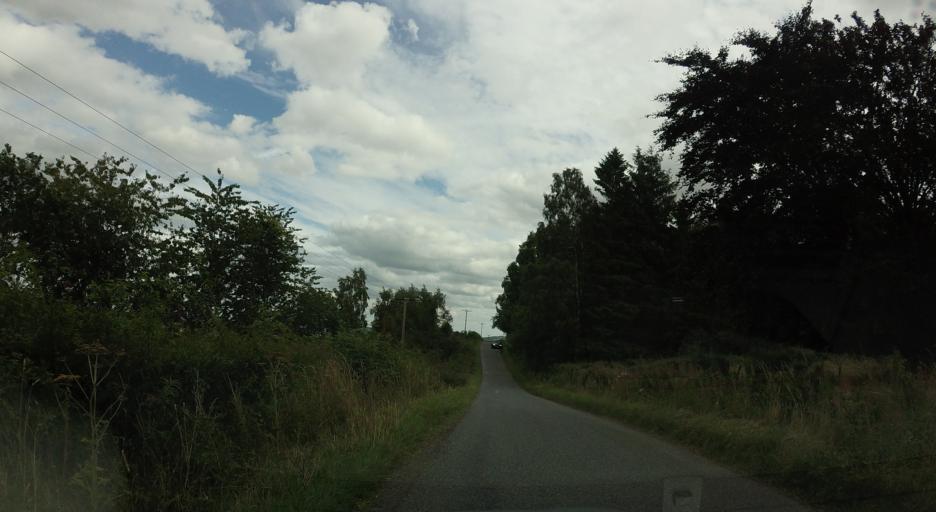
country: GB
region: Scotland
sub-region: Perth and Kinross
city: Bridge of Earn
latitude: 56.3691
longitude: -3.3795
